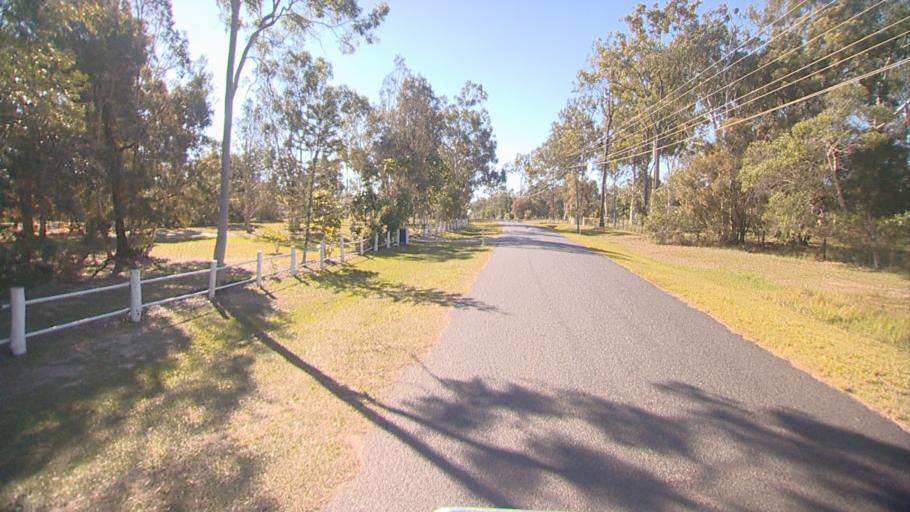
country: AU
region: Queensland
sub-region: Logan
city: Chambers Flat
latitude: -27.7331
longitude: 153.0717
